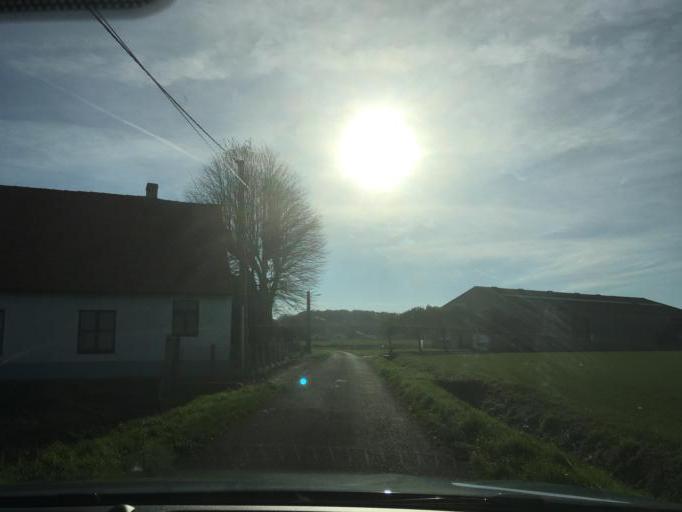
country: BE
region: Flanders
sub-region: Provincie West-Vlaanderen
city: Pittem
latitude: 50.9714
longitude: 3.2396
